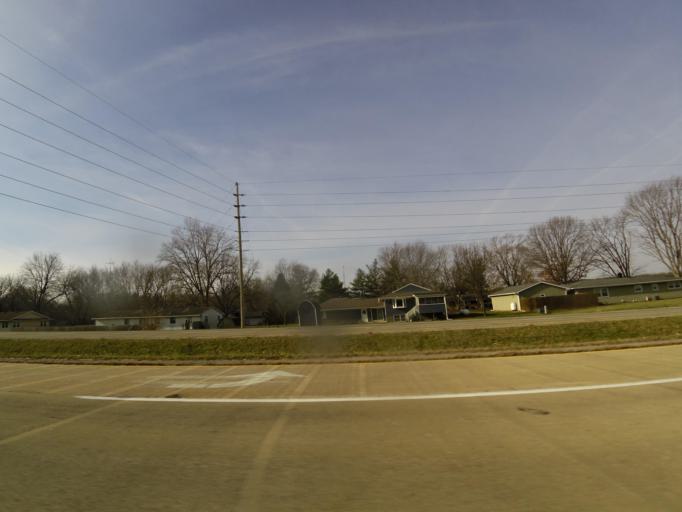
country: US
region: Illinois
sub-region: De Witt County
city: Clinton
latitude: 40.1023
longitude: -88.9652
